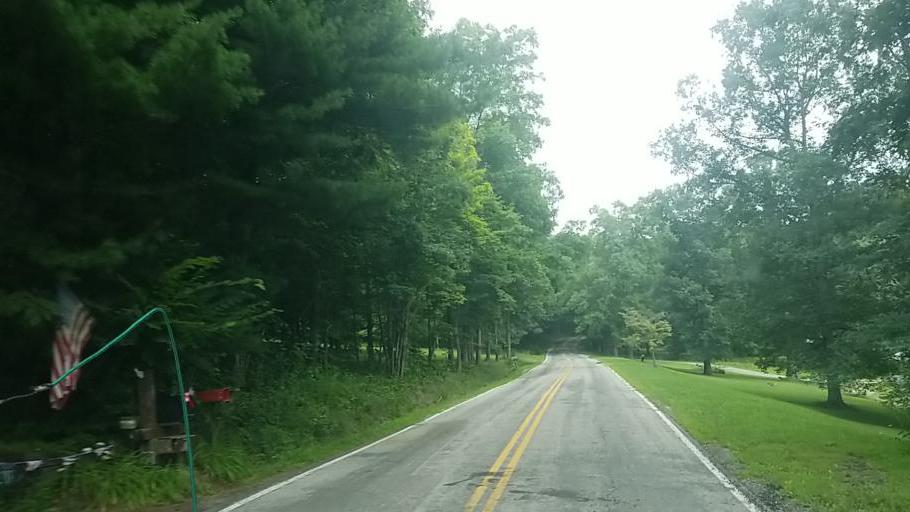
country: US
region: Ohio
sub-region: Muskingum County
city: Frazeysburg
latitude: 40.1695
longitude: -82.2604
